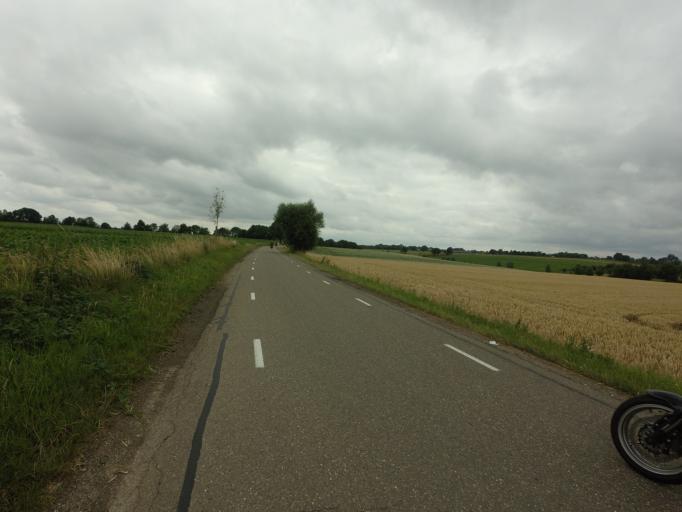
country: NL
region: Limburg
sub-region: Eijsden-Margraten
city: Margraten
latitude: 50.7919
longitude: 5.7889
